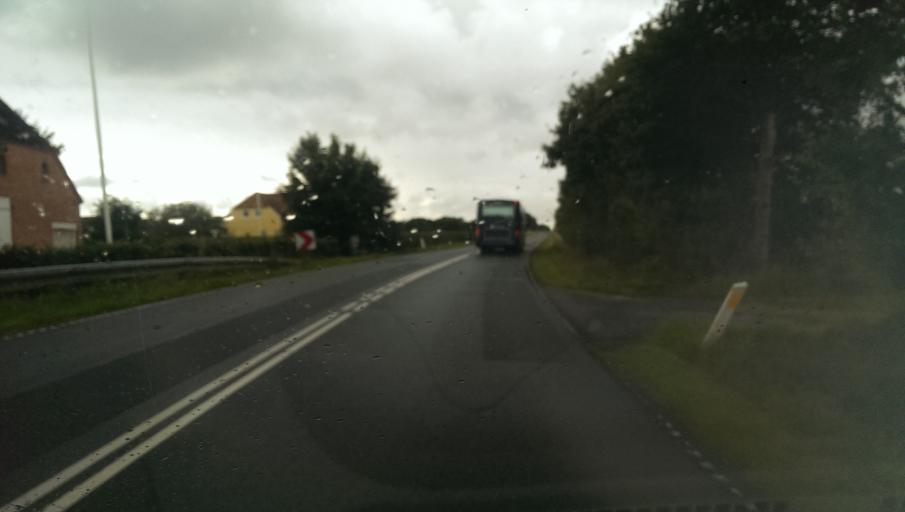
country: DK
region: South Denmark
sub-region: Esbjerg Kommune
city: Tjaereborg
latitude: 55.4899
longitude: 8.5913
